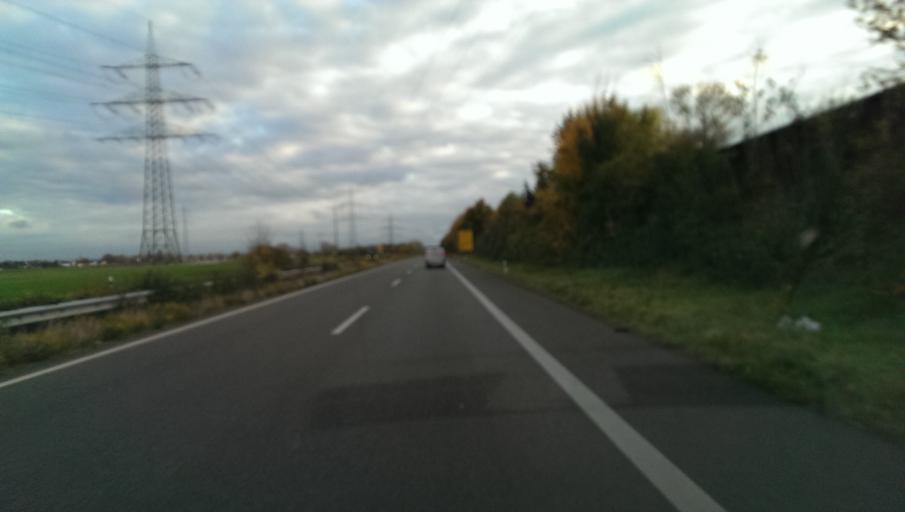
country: DE
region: Rheinland-Pfalz
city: Kuhardt
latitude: 49.1568
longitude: 8.3027
